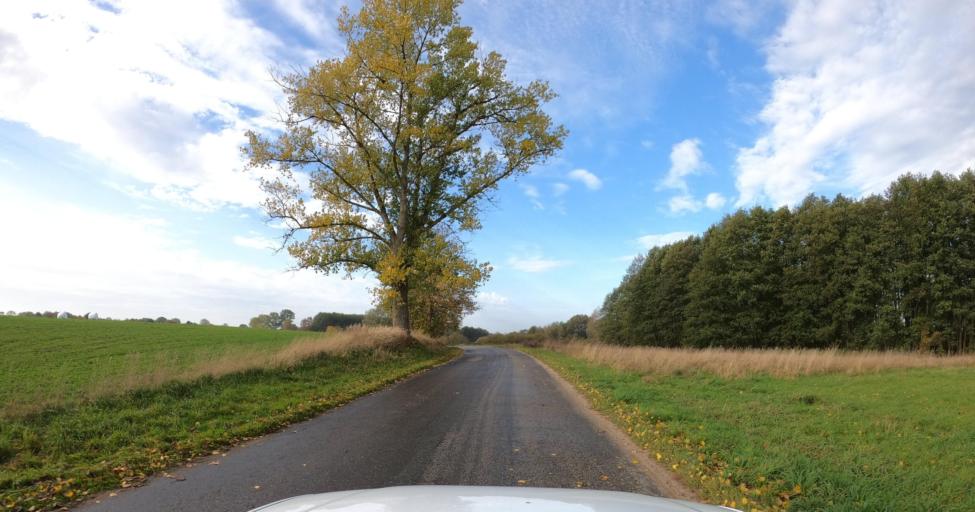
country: PL
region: West Pomeranian Voivodeship
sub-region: Powiat kamienski
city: Kamien Pomorski
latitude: 53.9630
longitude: 14.8250
